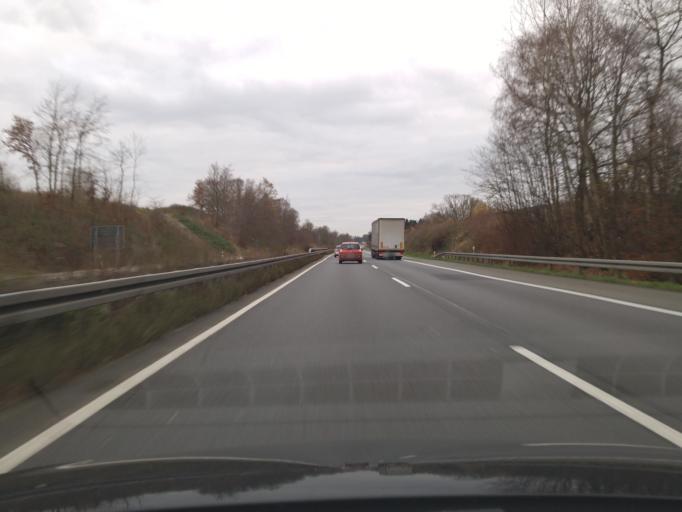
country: DE
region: Lower Saxony
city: Seesen
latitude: 51.8442
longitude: 10.1210
